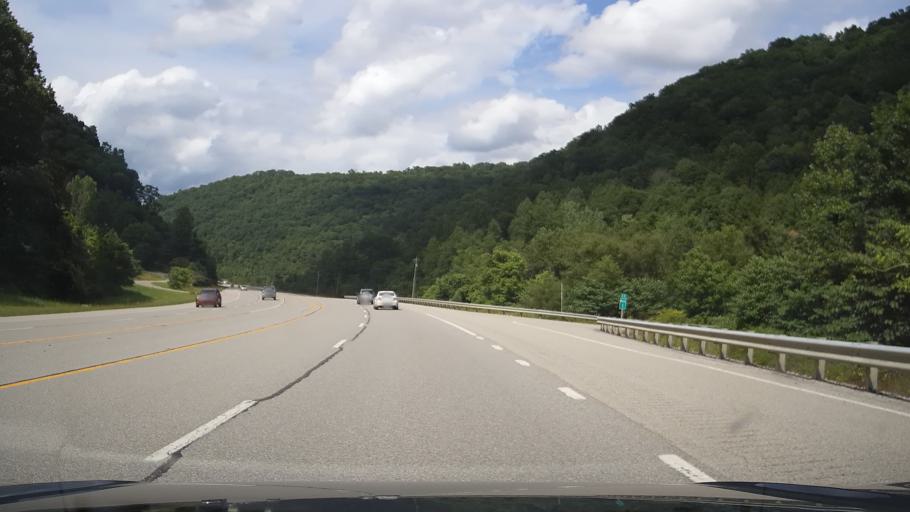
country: US
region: Kentucky
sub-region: Letcher County
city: Jenkins
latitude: 37.2528
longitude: -82.6155
